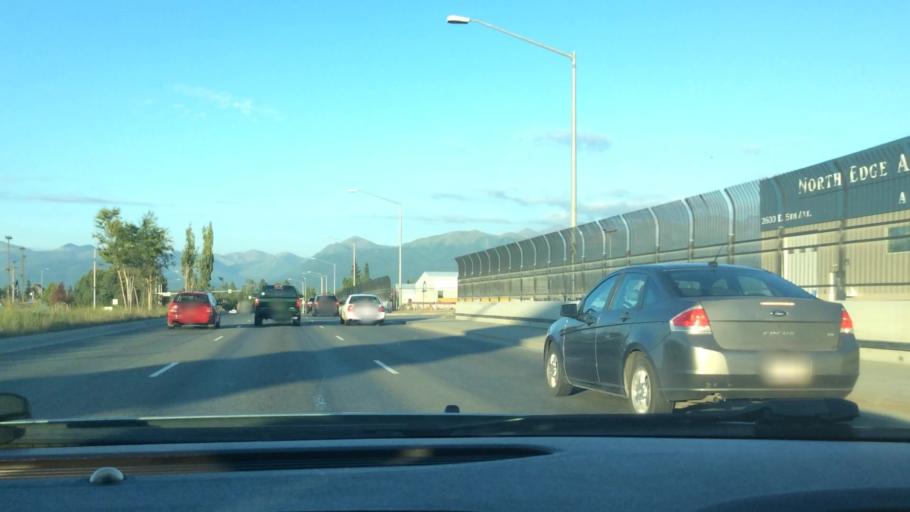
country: US
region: Alaska
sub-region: Anchorage Municipality
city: Anchorage
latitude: 61.2174
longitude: -149.8317
